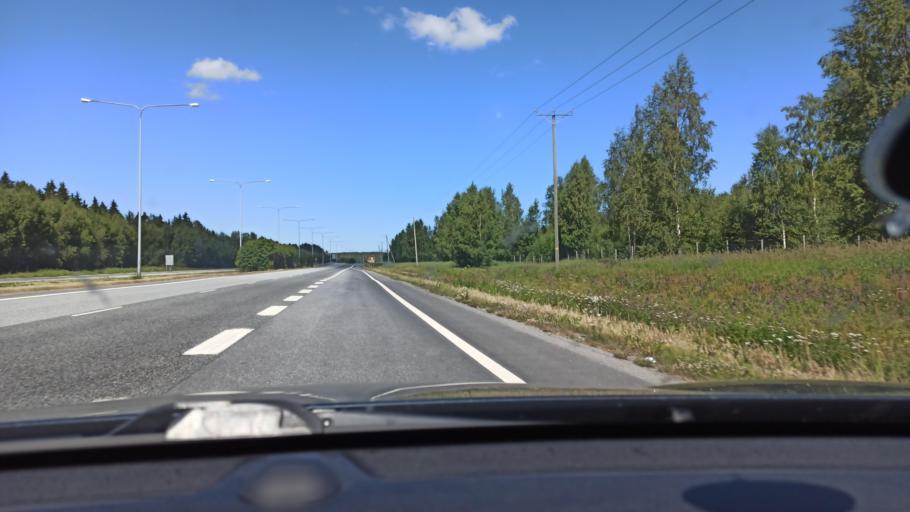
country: FI
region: Ostrobothnia
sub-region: Vaasa
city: Ristinummi
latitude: 63.0378
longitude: 21.7361
